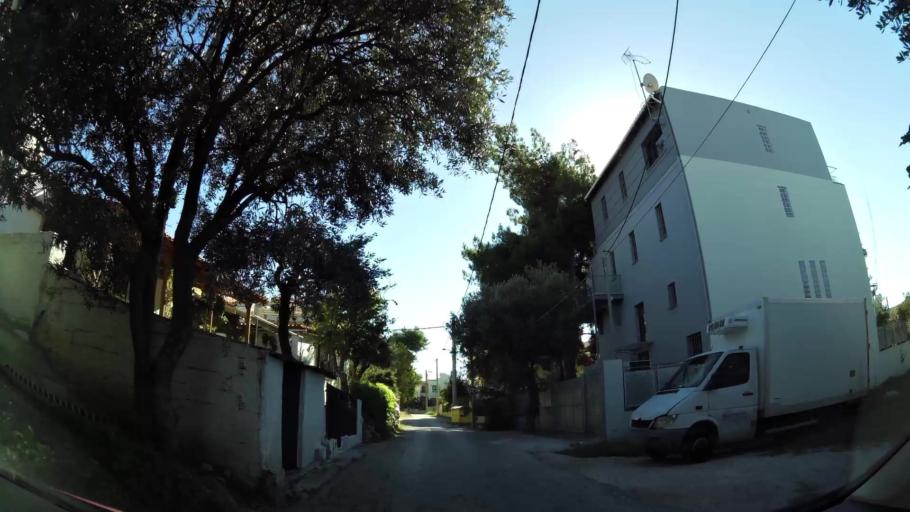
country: GR
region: Attica
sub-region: Nomarchia Athinas
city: Agia Paraskevi
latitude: 38.0198
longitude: 23.8414
